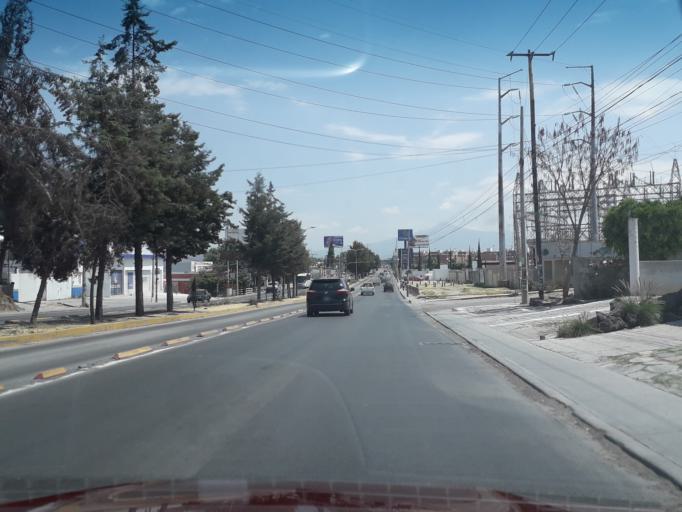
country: MX
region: Puebla
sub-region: Puebla
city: El Capulo (La Quebradora)
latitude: 18.9855
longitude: -98.2499
